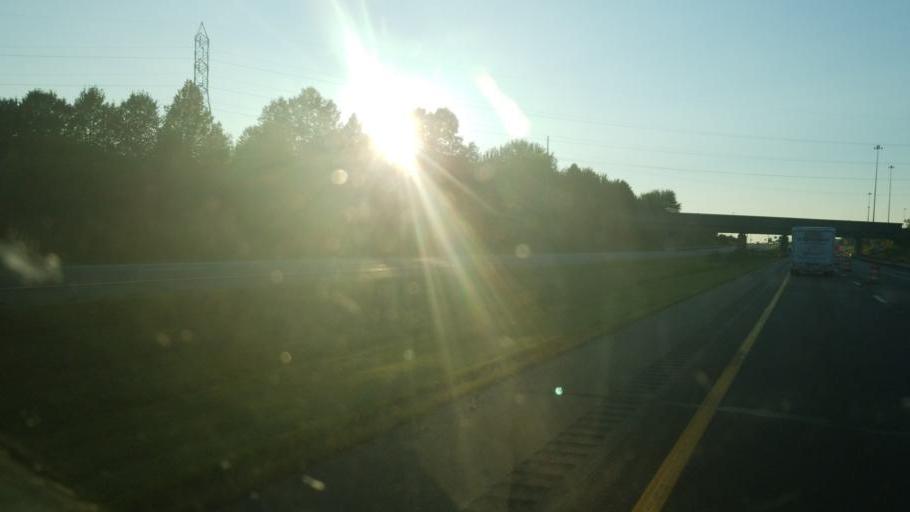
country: US
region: Ohio
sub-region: Mahoning County
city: Boardman
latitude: 40.9625
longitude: -80.6489
